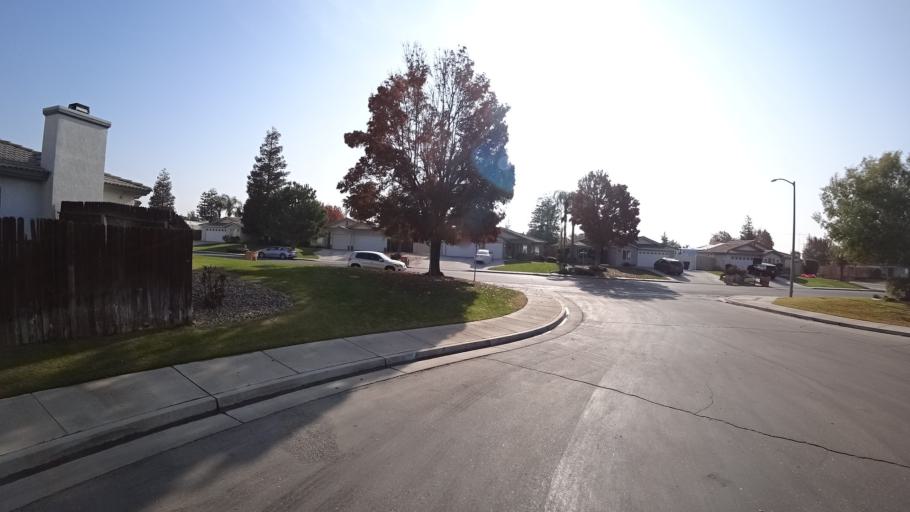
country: US
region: California
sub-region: Kern County
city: Greenacres
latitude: 35.4077
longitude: -119.1151
